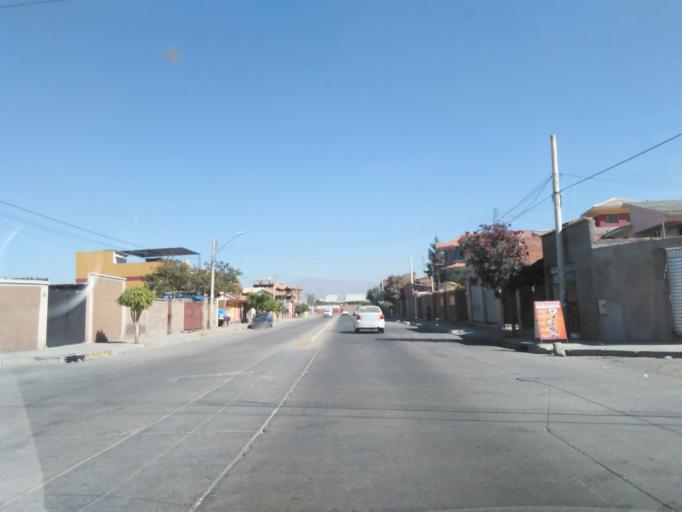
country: BO
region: Cochabamba
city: Cochabamba
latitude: -17.4010
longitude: -66.1844
